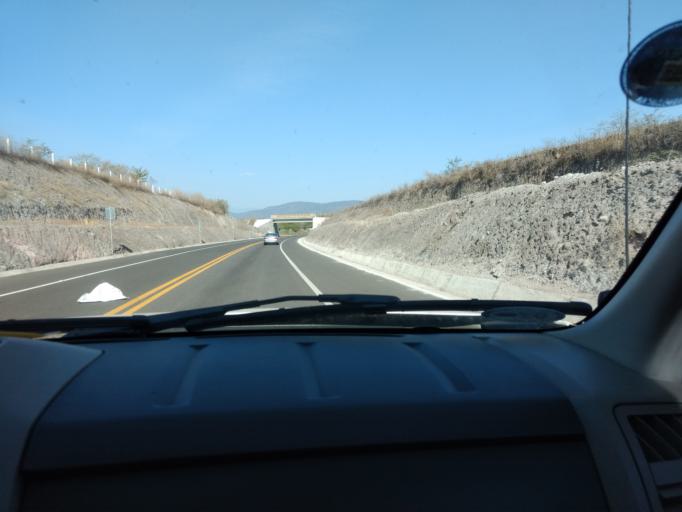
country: MX
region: Morelos
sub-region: Ayala
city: El Salitre
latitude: 18.6717
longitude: -98.9558
